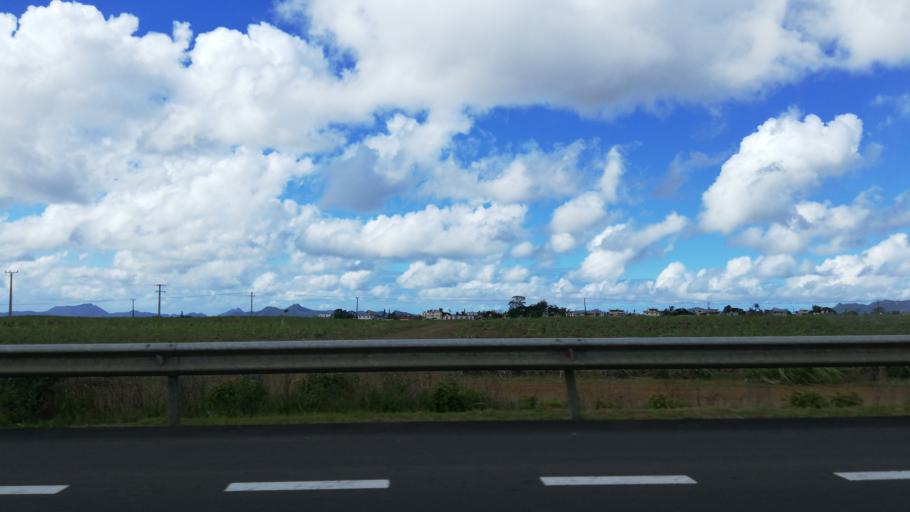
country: MU
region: Moka
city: Providence
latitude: -20.2428
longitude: 57.6171
